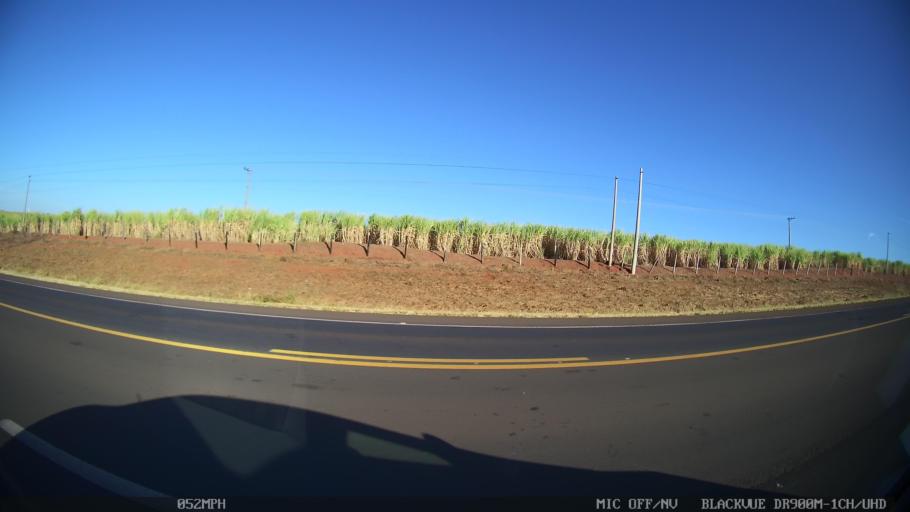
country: BR
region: Sao Paulo
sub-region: Olimpia
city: Olimpia
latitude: -20.6964
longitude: -48.9296
